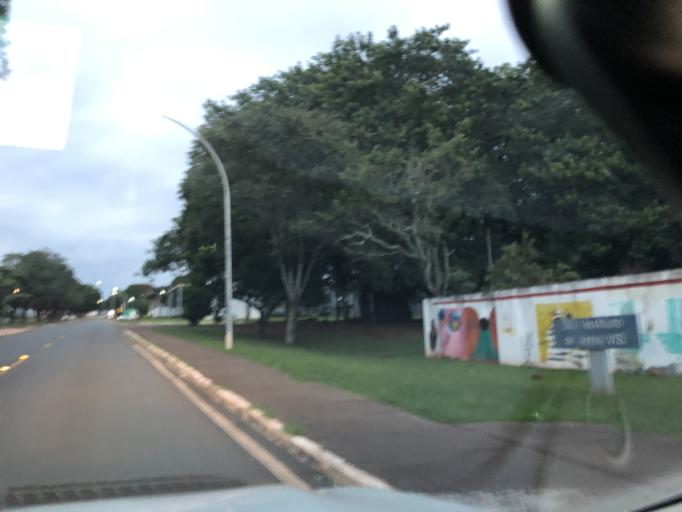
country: BR
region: Federal District
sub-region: Brasilia
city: Brasilia
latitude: -15.7660
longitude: -47.8700
